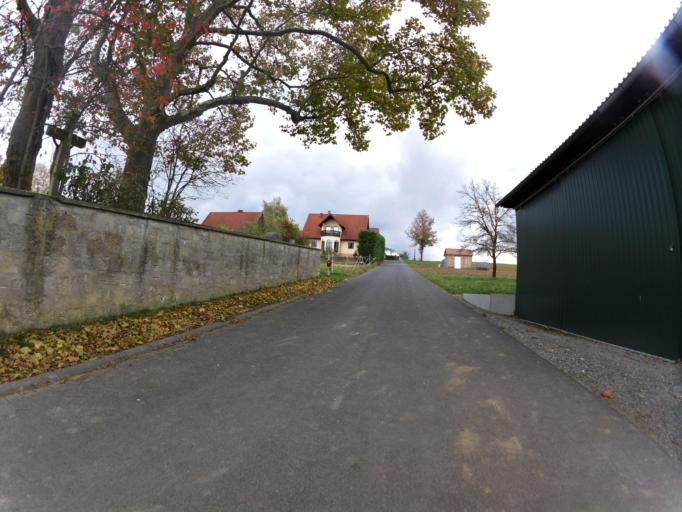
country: DE
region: Bavaria
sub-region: Regierungsbezirk Unterfranken
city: Kurnach
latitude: 49.8592
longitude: 10.0129
